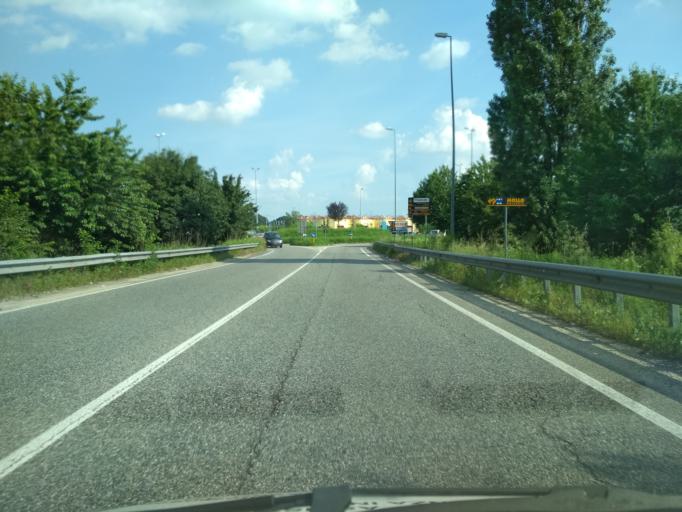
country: IT
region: Piedmont
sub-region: Provincia di Torino
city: Pasta
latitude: 45.0143
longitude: 7.5551
